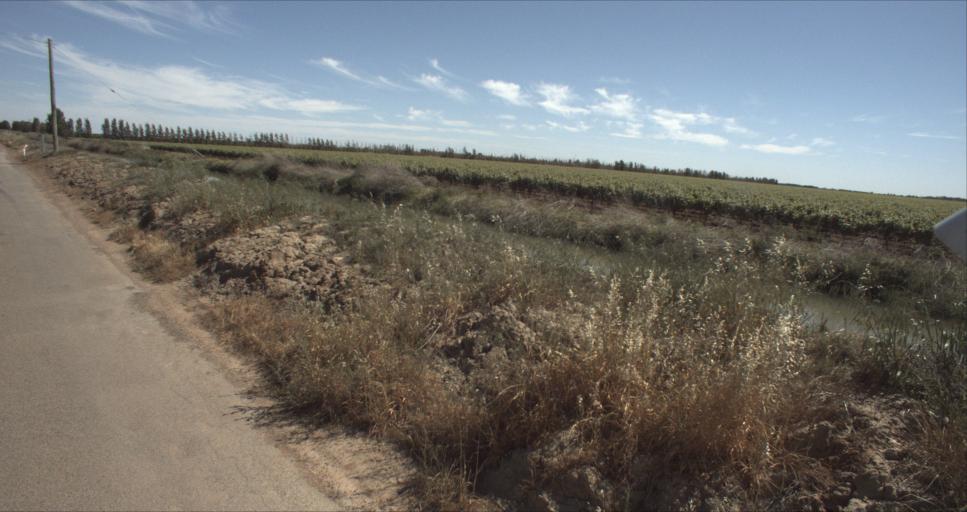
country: AU
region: New South Wales
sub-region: Leeton
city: Leeton
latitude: -34.5540
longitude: 146.3777
